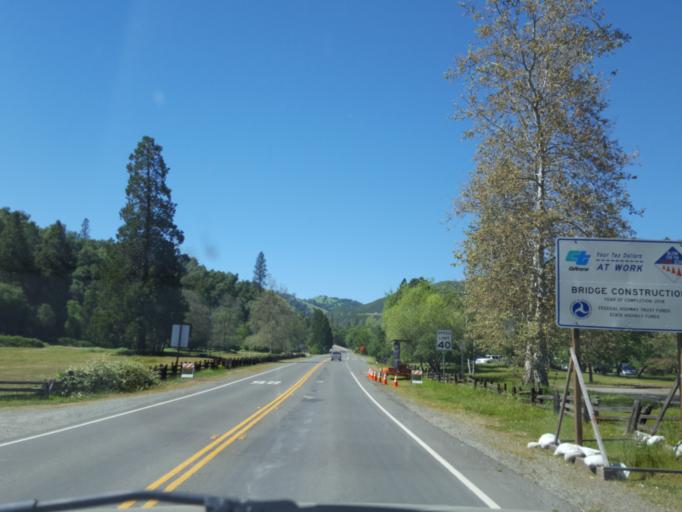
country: US
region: California
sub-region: El Dorado County
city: Georgetown
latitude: 38.8039
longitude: -120.8948
